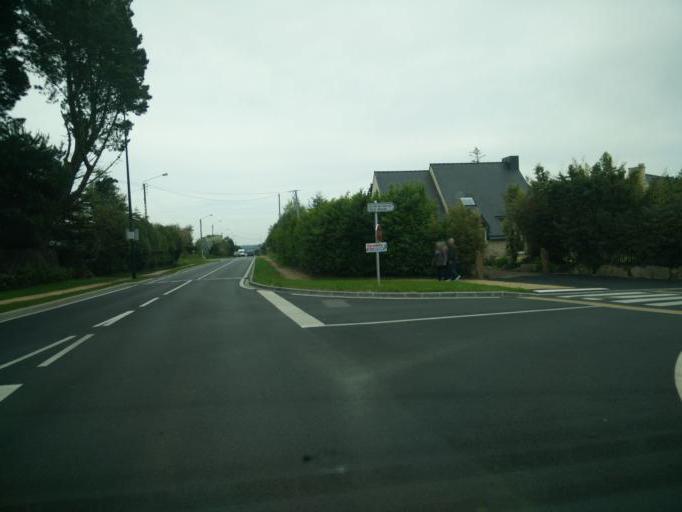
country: FR
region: Brittany
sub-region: Departement des Cotes-d'Armor
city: Pleumeur-Bodou
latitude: 48.7504
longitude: -3.4917
